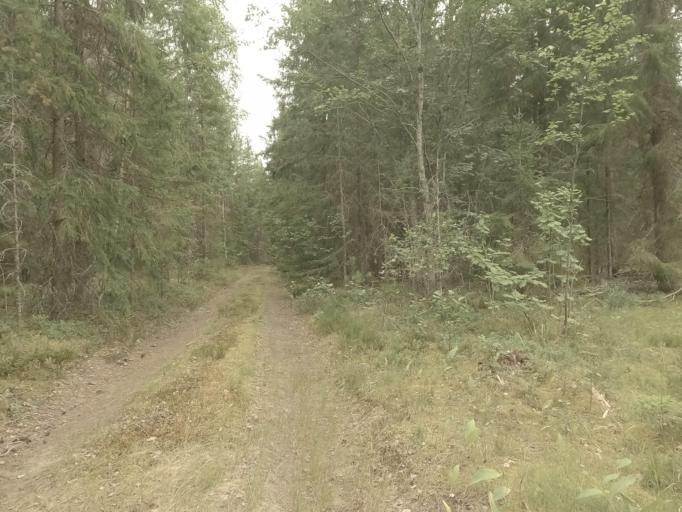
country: RU
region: Leningrad
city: Kamennogorsk
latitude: 61.0431
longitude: 29.1864
